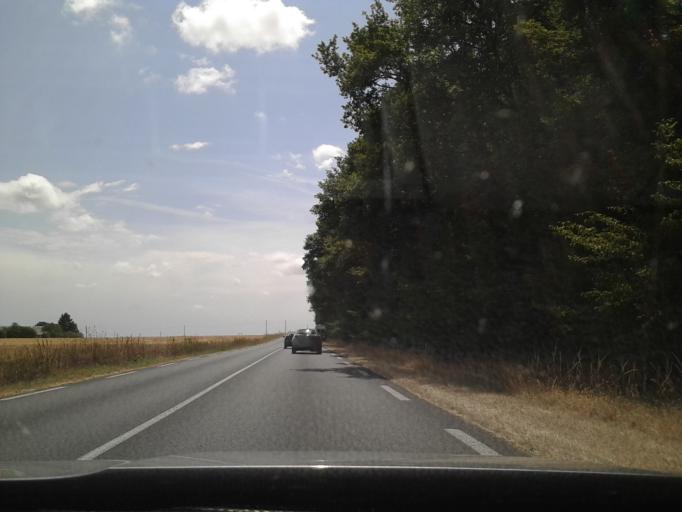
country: FR
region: Centre
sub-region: Departement d'Indre-et-Loire
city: Poce-sur-Cisse
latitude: 47.4972
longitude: 1.0055
